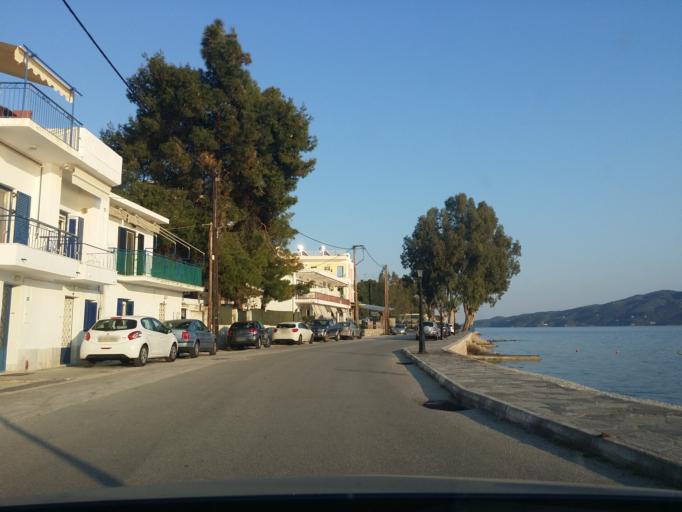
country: GR
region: Attica
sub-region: Nomos Piraios
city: Poros
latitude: 37.5070
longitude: 23.4723
